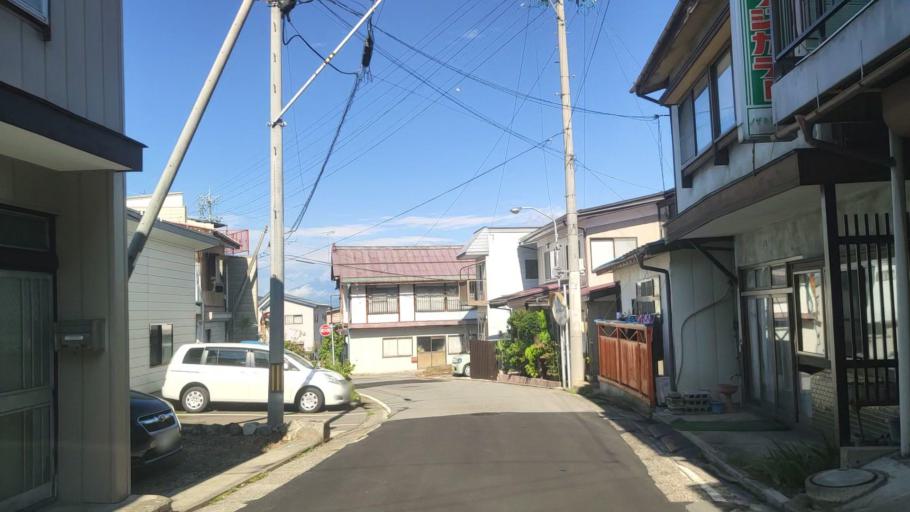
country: JP
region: Nagano
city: Nakano
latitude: 36.7396
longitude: 138.4193
